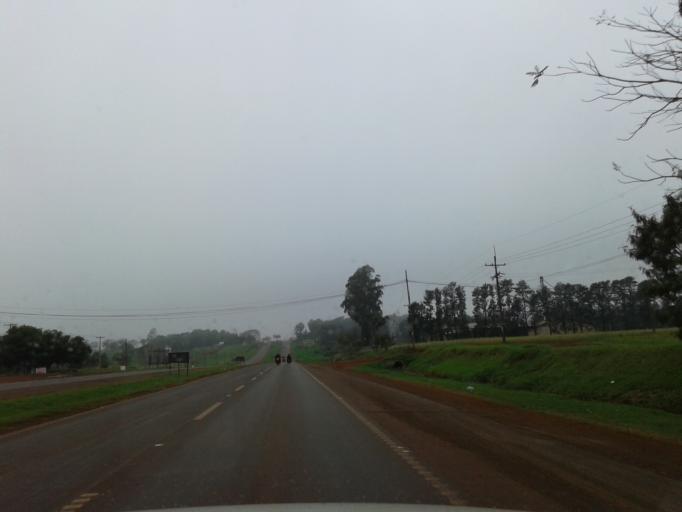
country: PY
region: Alto Parana
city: Colonia Yguazu
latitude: -25.4858
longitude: -54.8803
